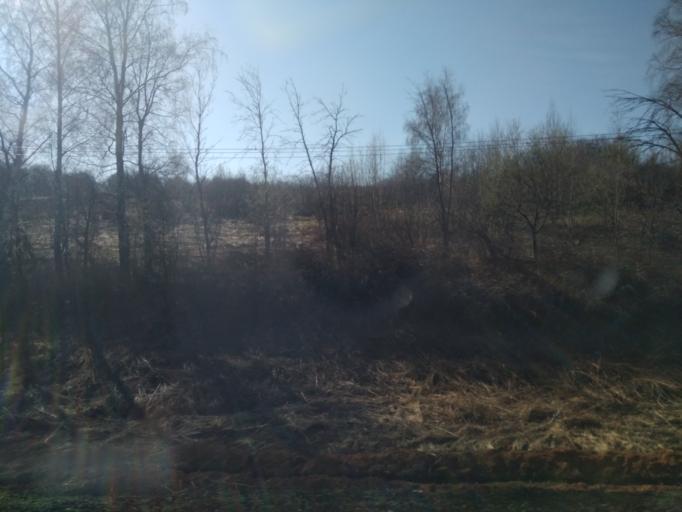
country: RU
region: Moskovskaya
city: Pavshino
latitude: 55.8243
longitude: 37.3616
